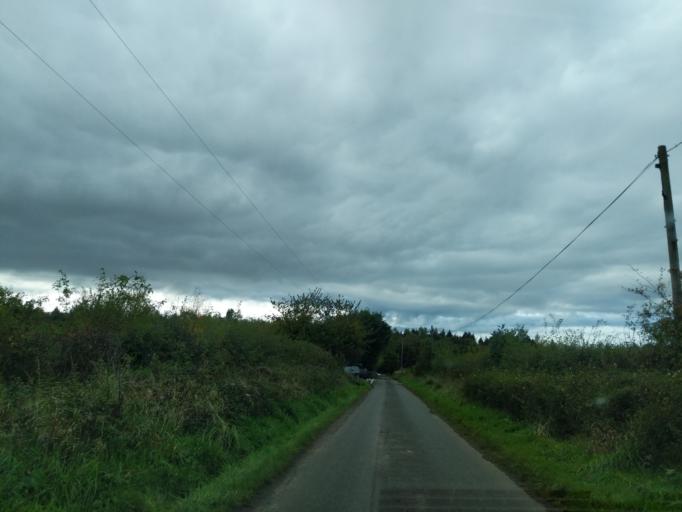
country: GB
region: Scotland
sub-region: East Lothian
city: Macmerry
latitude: 55.9439
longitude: -2.8624
